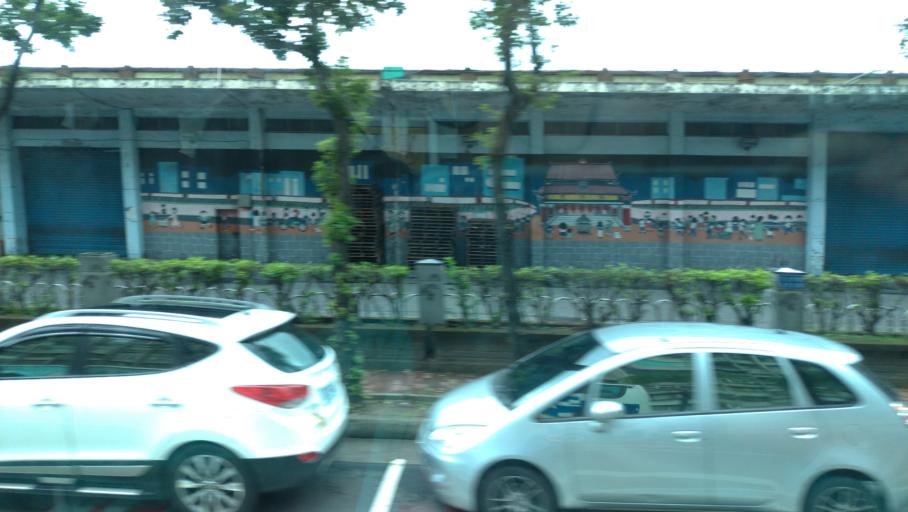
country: TW
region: Taiwan
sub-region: Keelung
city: Keelung
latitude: 25.1384
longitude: 121.7504
